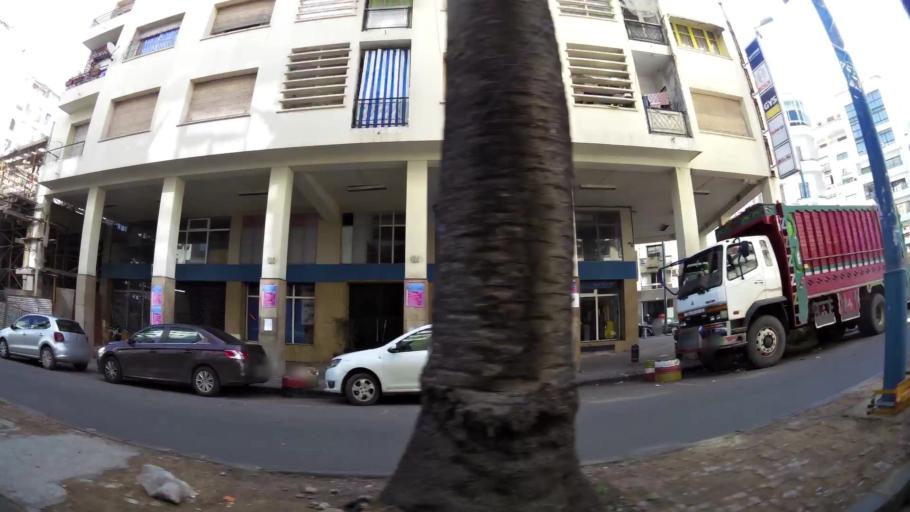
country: MA
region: Grand Casablanca
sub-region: Casablanca
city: Casablanca
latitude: 33.5902
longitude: -7.6084
